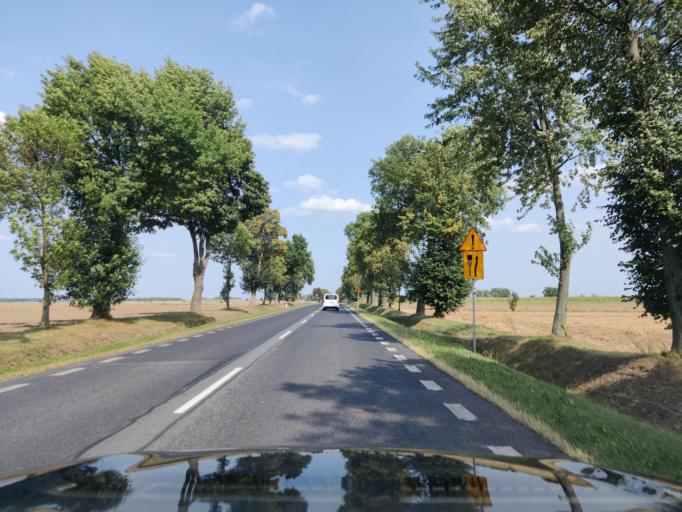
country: PL
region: Masovian Voivodeship
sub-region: Powiat makowski
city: Rzewnie
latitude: 52.8588
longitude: 21.3102
